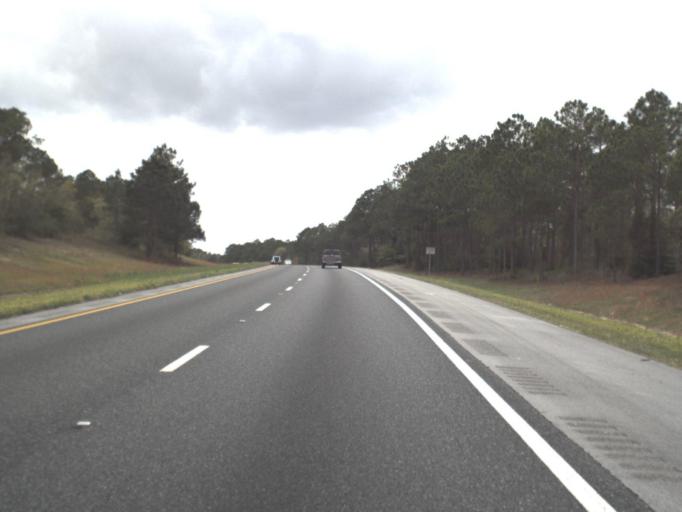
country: US
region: Florida
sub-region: Okaloosa County
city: Crestview
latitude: 30.7254
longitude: -86.5862
